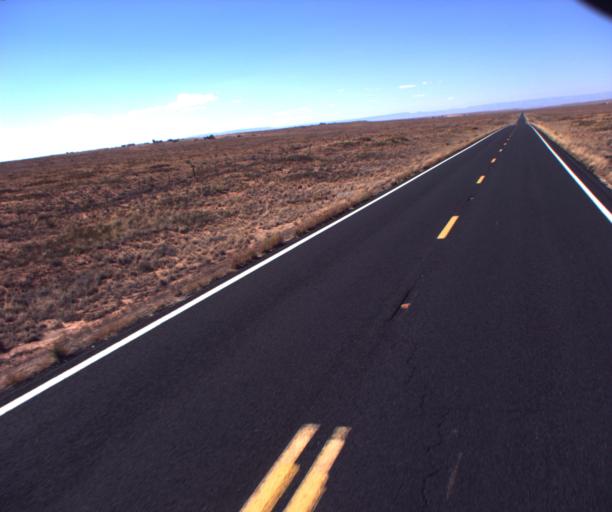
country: US
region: Arizona
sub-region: Coconino County
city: Tuba City
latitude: 36.0124
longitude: -111.0780
